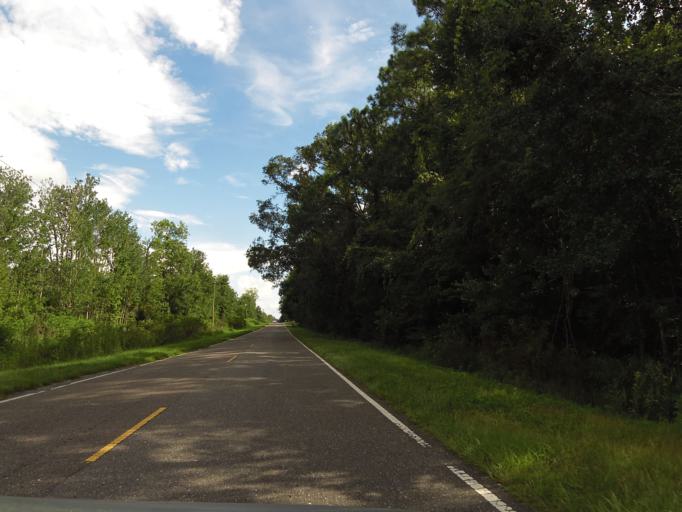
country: US
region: Florida
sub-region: Clay County
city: Green Cove Springs
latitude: 29.9658
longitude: -81.6934
